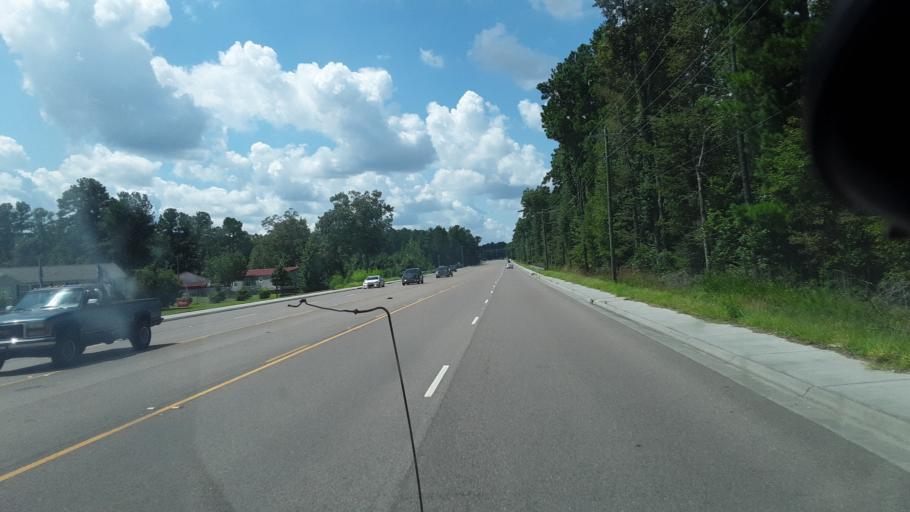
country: US
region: South Carolina
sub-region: Berkeley County
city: Moncks Corner
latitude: 33.1642
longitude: -80.0504
